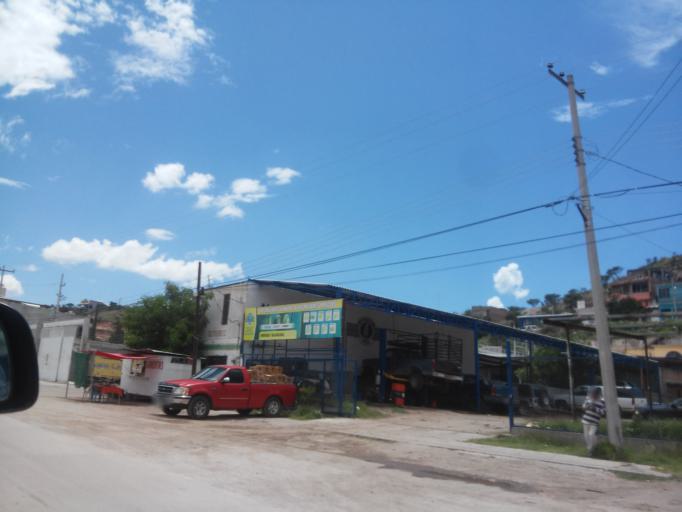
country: MX
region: Durango
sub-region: Santiago Papasquiaro
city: Santiago Papasquiaro
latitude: 25.0532
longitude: -105.4243
